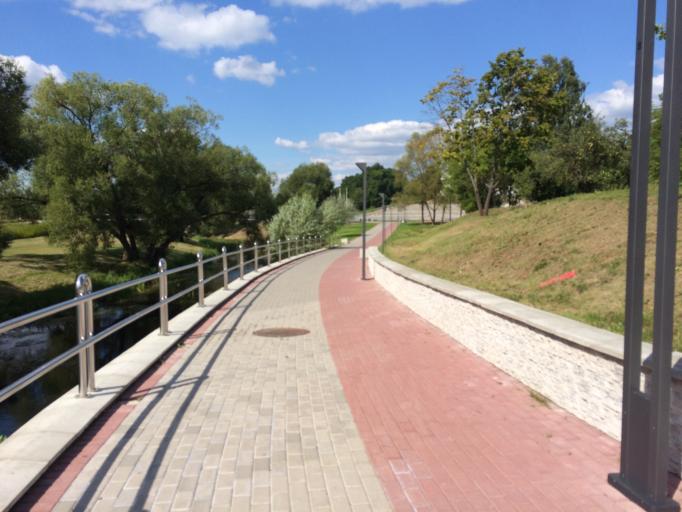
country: LV
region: Rezekne
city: Rezekne
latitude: 56.5027
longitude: 27.3277
